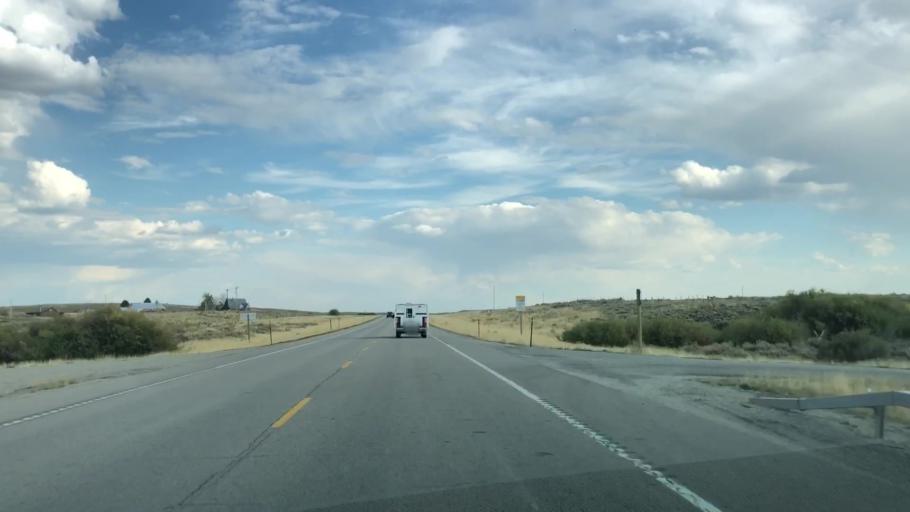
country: US
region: Wyoming
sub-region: Sublette County
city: Pinedale
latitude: 43.0183
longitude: -110.1183
